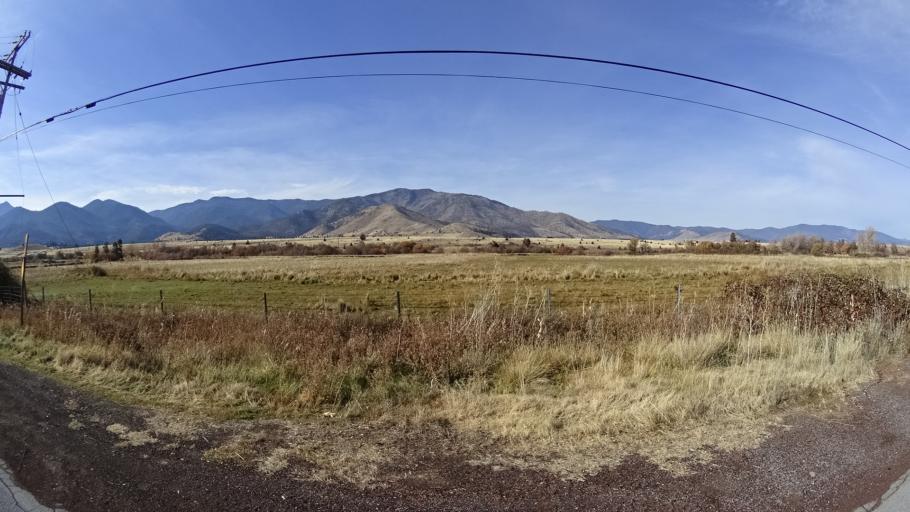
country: US
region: California
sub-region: Siskiyou County
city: Weed
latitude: 41.4682
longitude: -122.4347
